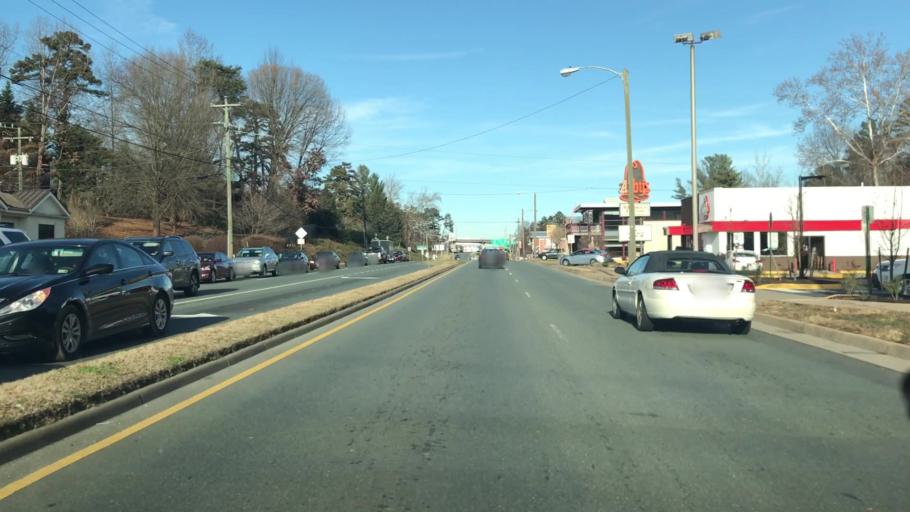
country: US
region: Virginia
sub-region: City of Charlottesville
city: Charlottesville
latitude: 38.0534
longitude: -78.4984
